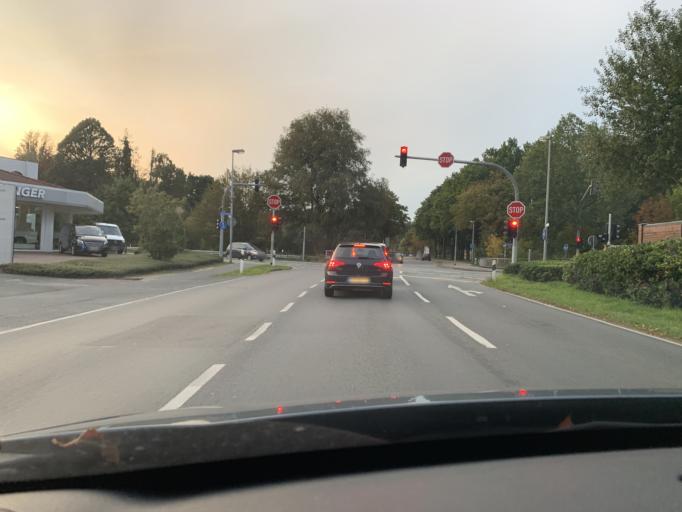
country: DE
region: Lower Saxony
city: Westerstede
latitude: 53.2518
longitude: 7.9156
